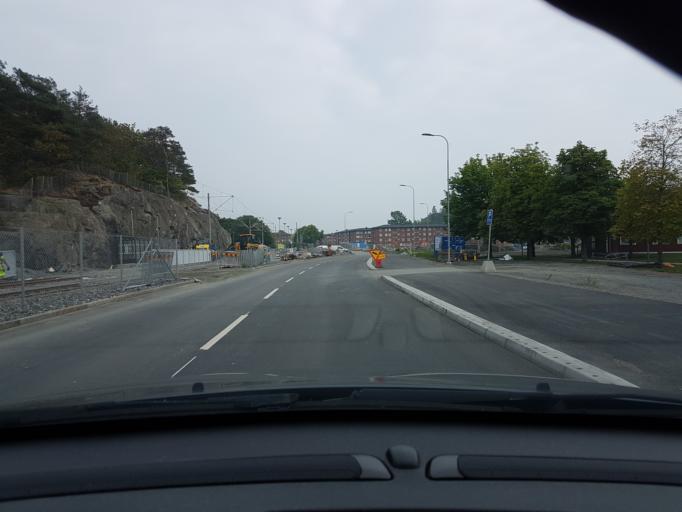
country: SE
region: Vaestra Goetaland
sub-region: Goteborg
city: Majorna
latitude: 57.6433
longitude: 11.8994
